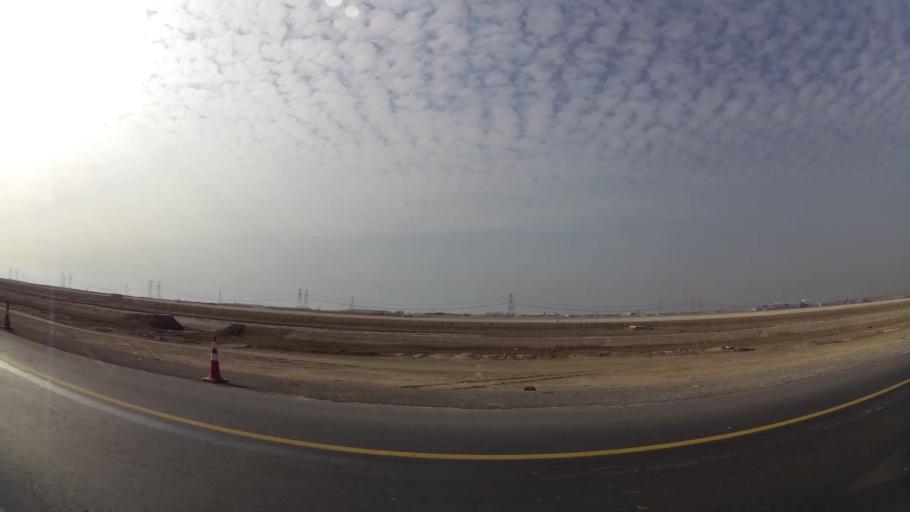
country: AE
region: Abu Dhabi
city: Abu Dhabi
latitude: 24.2582
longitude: 54.4854
